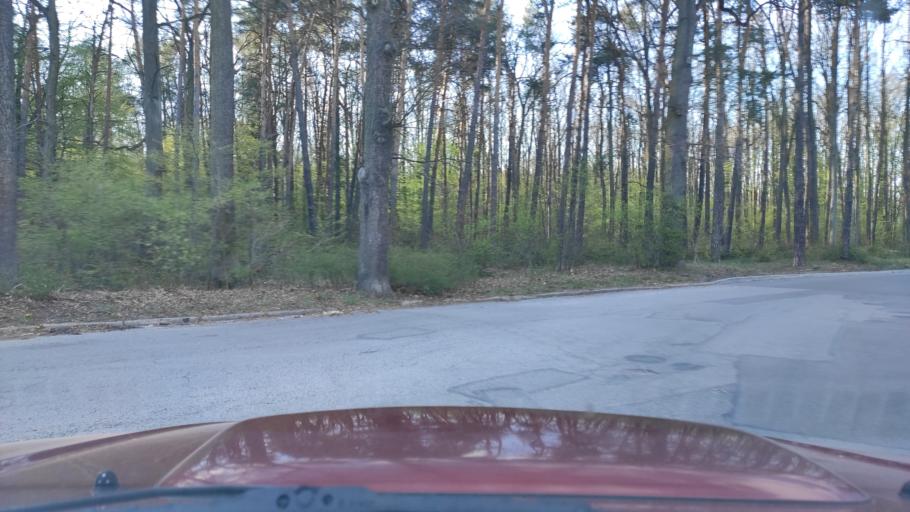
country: PL
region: Masovian Voivodeship
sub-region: Powiat radomski
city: Pionki
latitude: 51.4736
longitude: 21.4389
